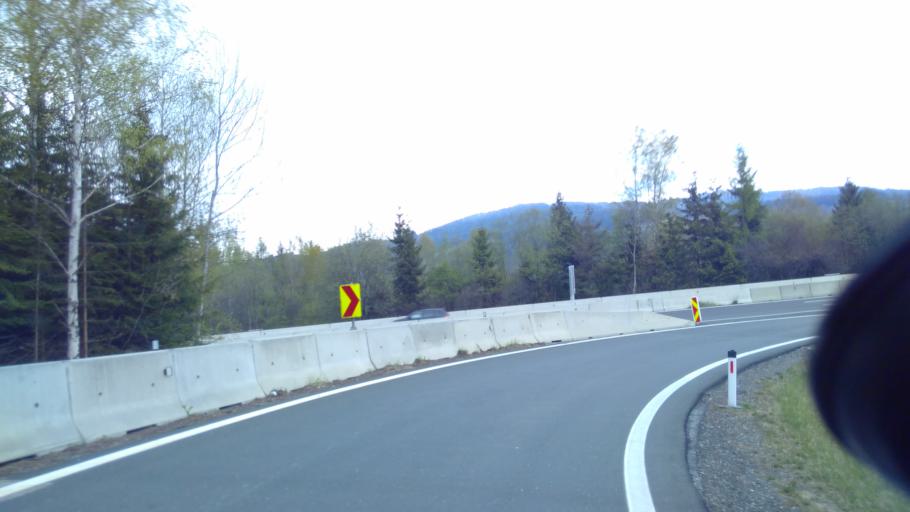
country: AT
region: Carinthia
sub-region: Politischer Bezirk Wolfsberg
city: Bad Sankt Leonhard im Lavanttal
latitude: 46.9345
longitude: 14.8535
